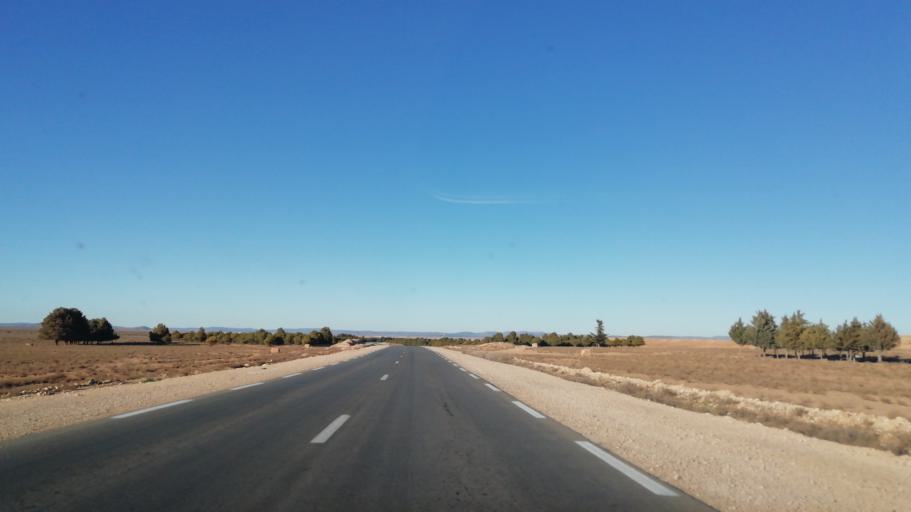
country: DZ
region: Tlemcen
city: Sebdou
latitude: 34.4487
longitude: -1.2754
